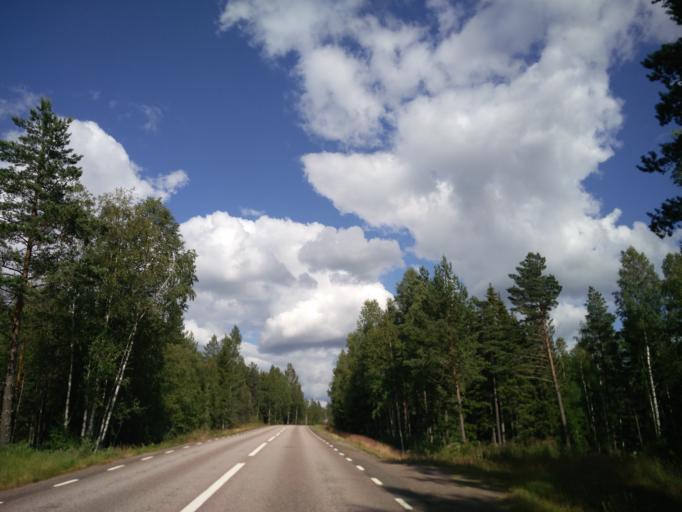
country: SE
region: Vaermland
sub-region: Sunne Kommun
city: Sunne
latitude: 59.6898
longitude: 13.0548
